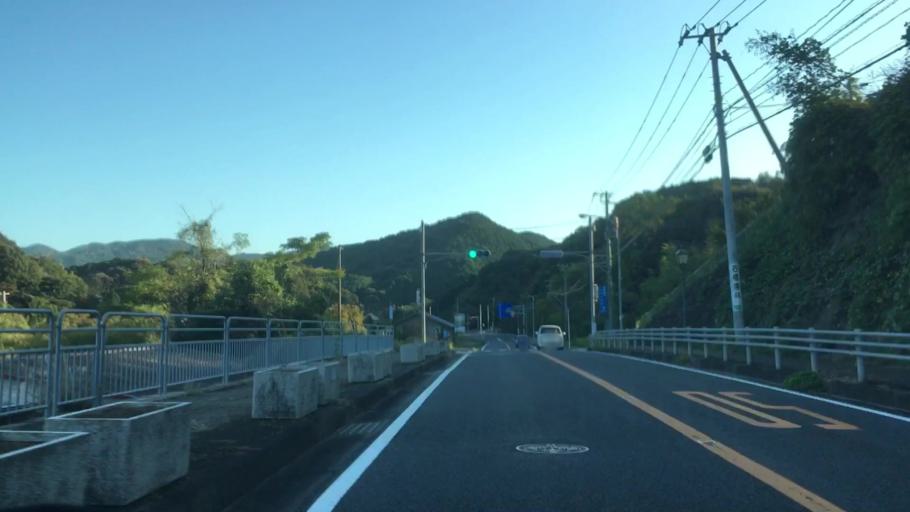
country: JP
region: Nagasaki
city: Sasebo
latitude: 32.9994
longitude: 129.7321
